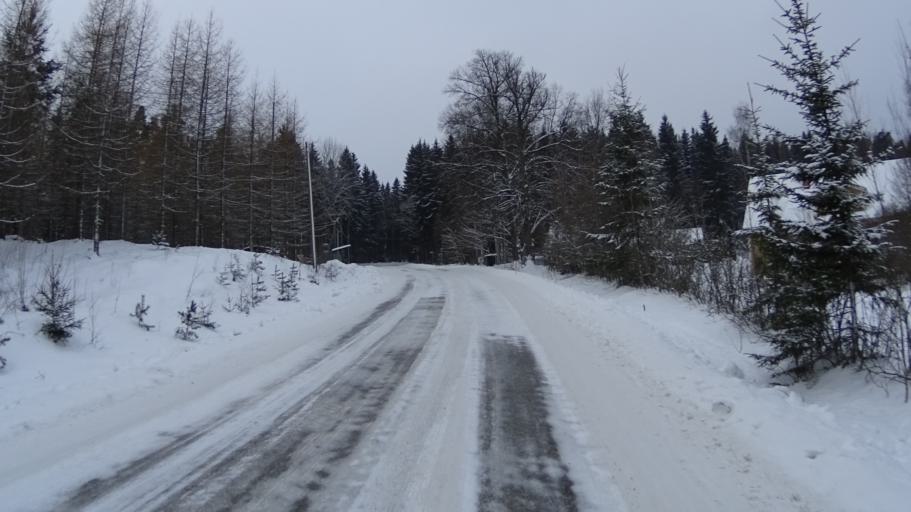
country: FI
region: Uusimaa
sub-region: Helsinki
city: Vihti
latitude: 60.3367
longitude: 24.2731
